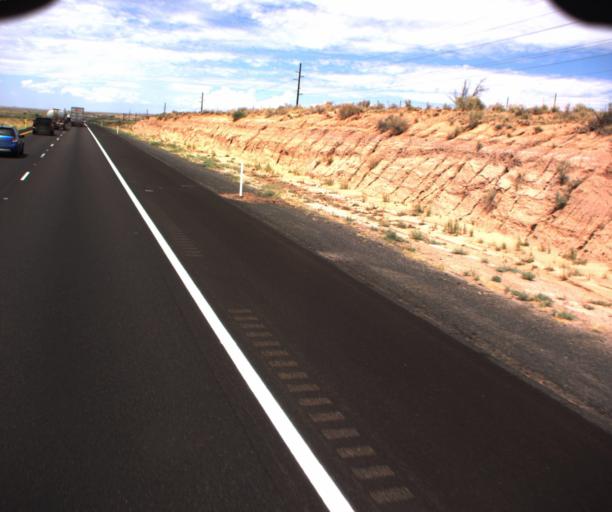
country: US
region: Arizona
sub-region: Navajo County
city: Holbrook
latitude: 34.9956
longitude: -109.9289
